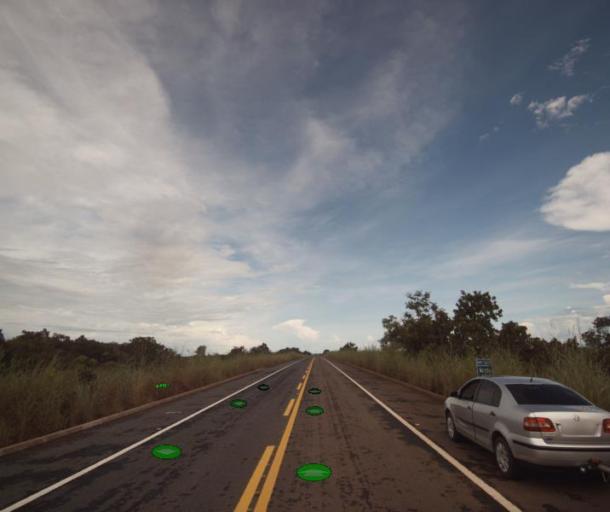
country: BR
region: Goias
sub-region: Sao Miguel Do Araguaia
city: Sao Miguel do Araguaia
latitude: -13.2761
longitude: -50.5004
